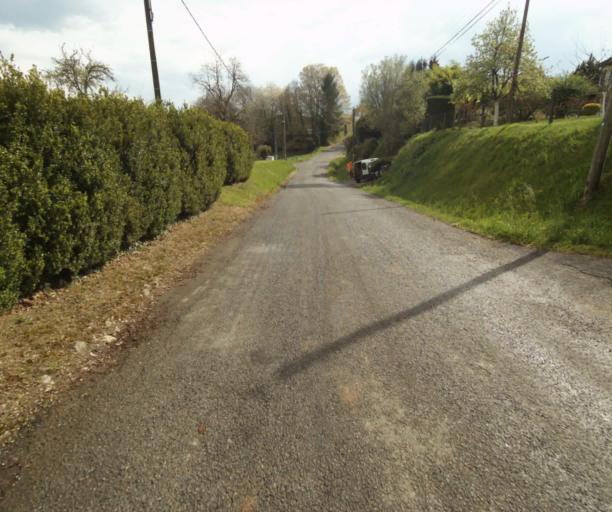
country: FR
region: Limousin
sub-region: Departement de la Correze
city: Tulle
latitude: 45.2841
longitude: 1.7521
